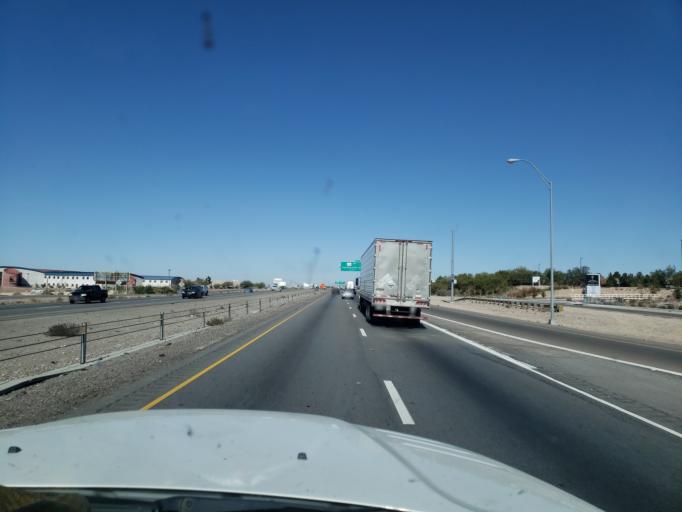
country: US
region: Texas
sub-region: El Paso County
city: Canutillo
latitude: 31.8932
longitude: -106.5828
